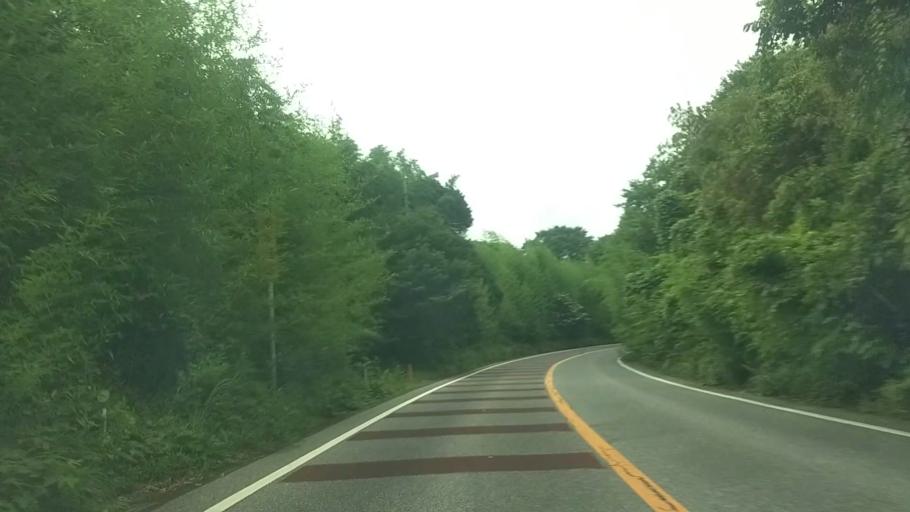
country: JP
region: Chiba
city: Kimitsu
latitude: 35.2360
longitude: 140.0068
